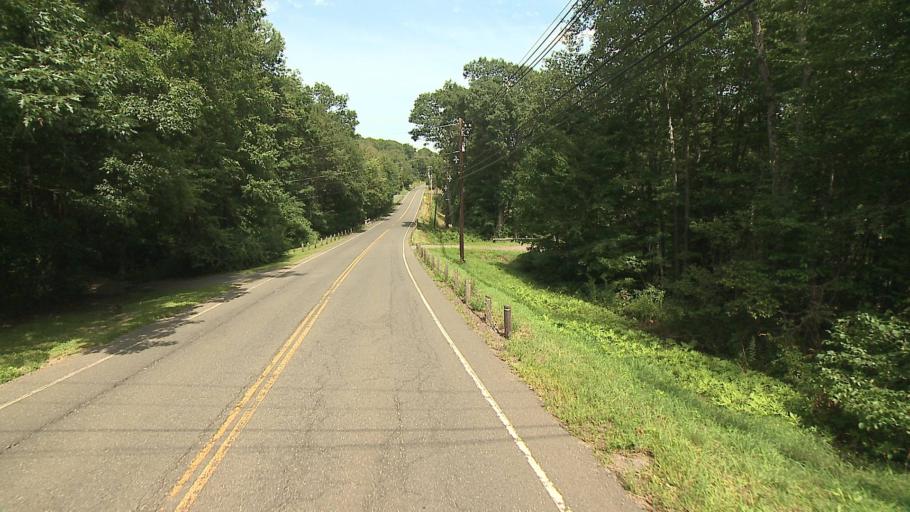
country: US
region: Connecticut
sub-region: Litchfield County
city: Bethlehem Village
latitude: 41.6266
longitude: -73.2259
